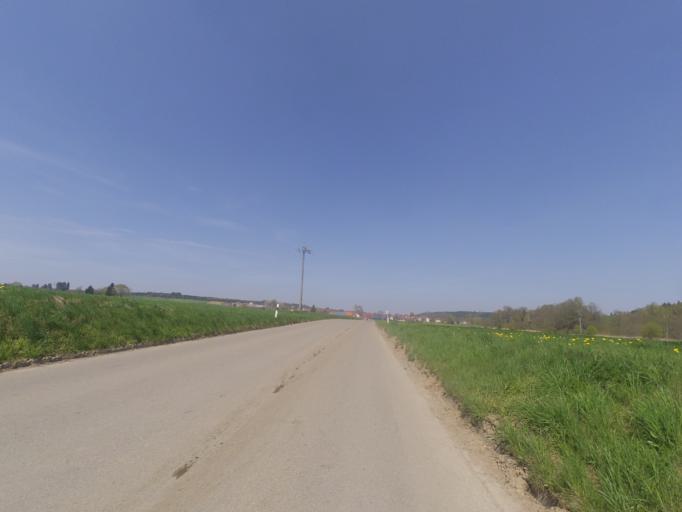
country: DE
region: Bavaria
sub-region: Swabia
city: Roggenburg
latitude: 48.2800
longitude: 10.2147
